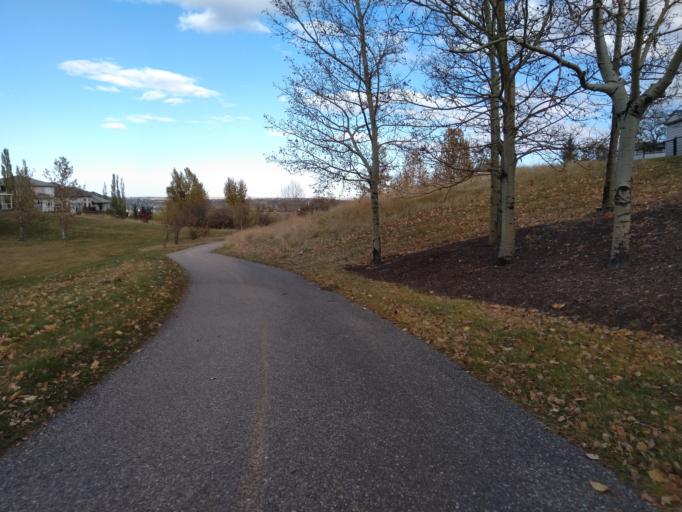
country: CA
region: Alberta
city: Calgary
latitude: 51.1388
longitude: -114.1275
